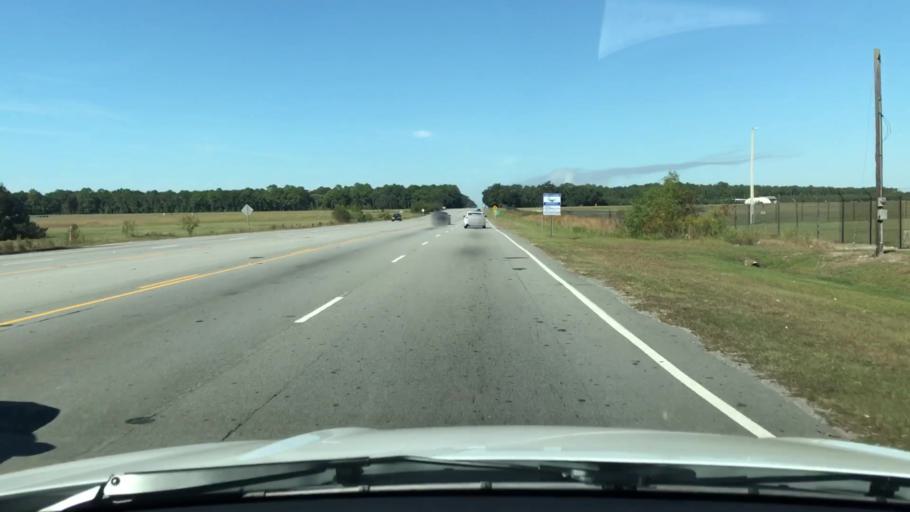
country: US
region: South Carolina
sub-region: Beaufort County
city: Burton
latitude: 32.4631
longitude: -80.7348
